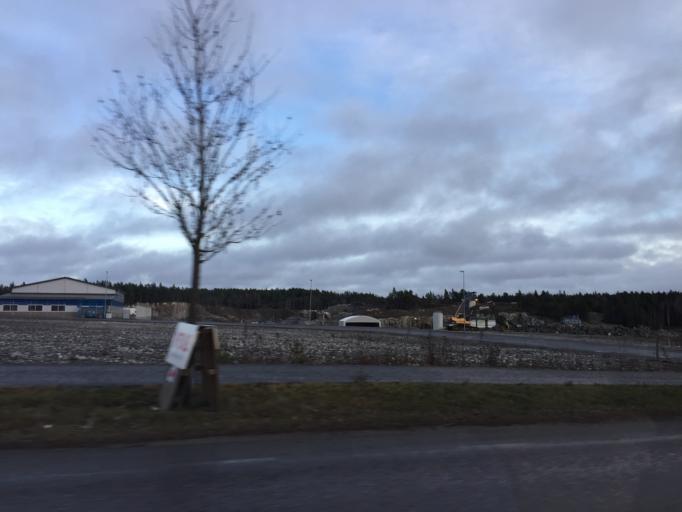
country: SE
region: Stockholm
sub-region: Sodertalje Kommun
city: Soedertaelje
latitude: 59.2055
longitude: 17.6642
